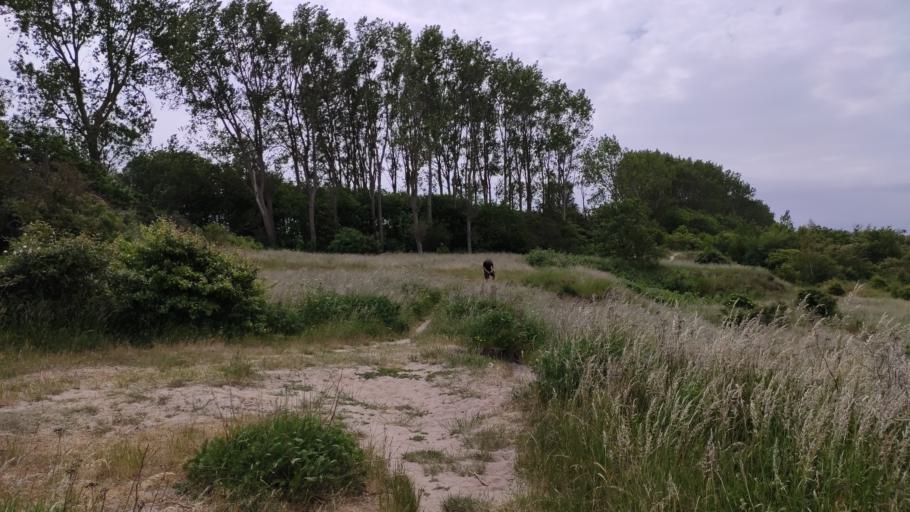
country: DE
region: Mecklenburg-Vorpommern
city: Bastorf
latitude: 54.1337
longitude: 11.6518
